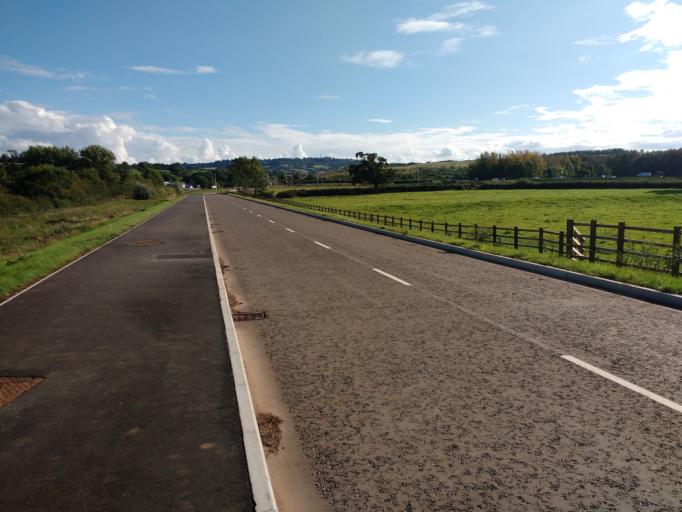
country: GB
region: England
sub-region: North Somerset
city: Long Ashton
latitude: 51.4335
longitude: -2.6339
